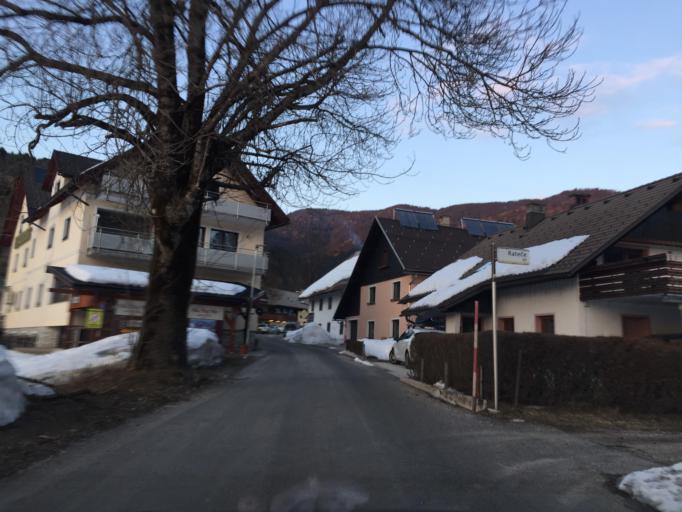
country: AT
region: Carinthia
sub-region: Politischer Bezirk Villach Land
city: Arnoldstein
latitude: 46.4971
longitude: 13.7120
